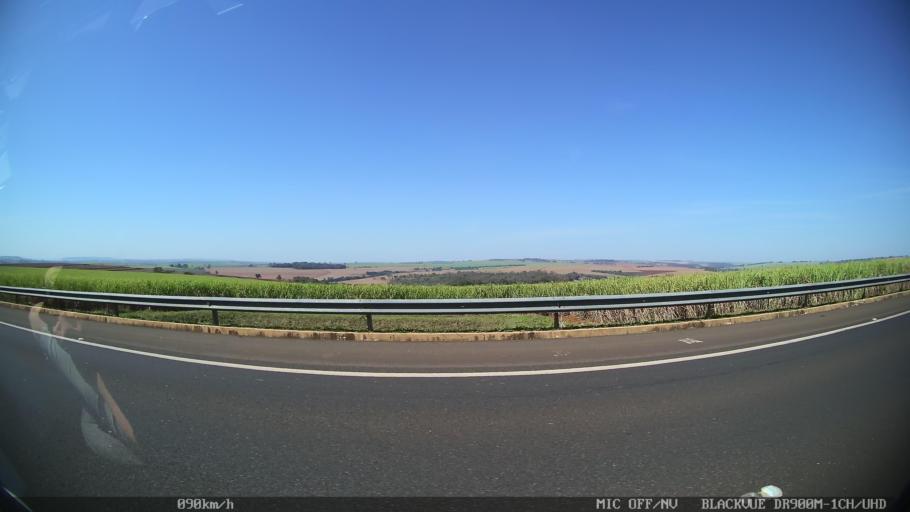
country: BR
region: Sao Paulo
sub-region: Batatais
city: Batatais
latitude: -20.7671
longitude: -47.5370
